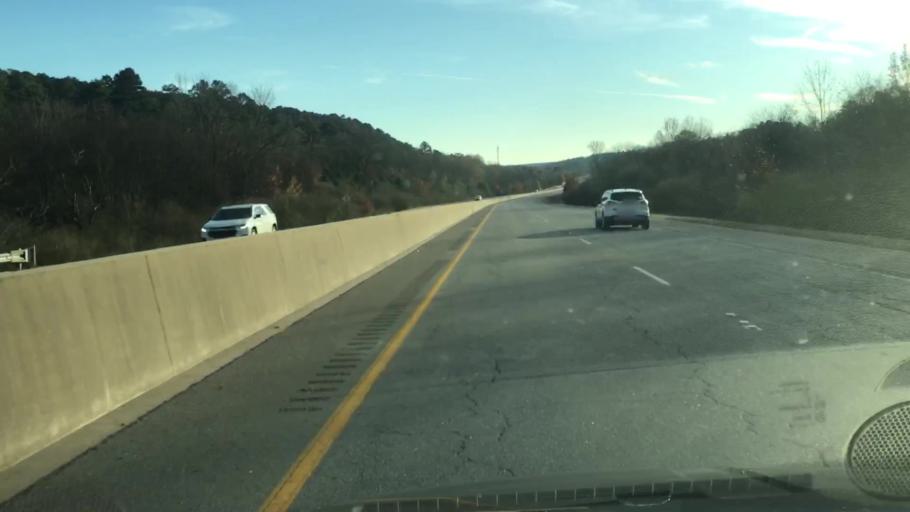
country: US
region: Arkansas
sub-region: Garland County
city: Hot Springs
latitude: 34.4842
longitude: -92.9818
